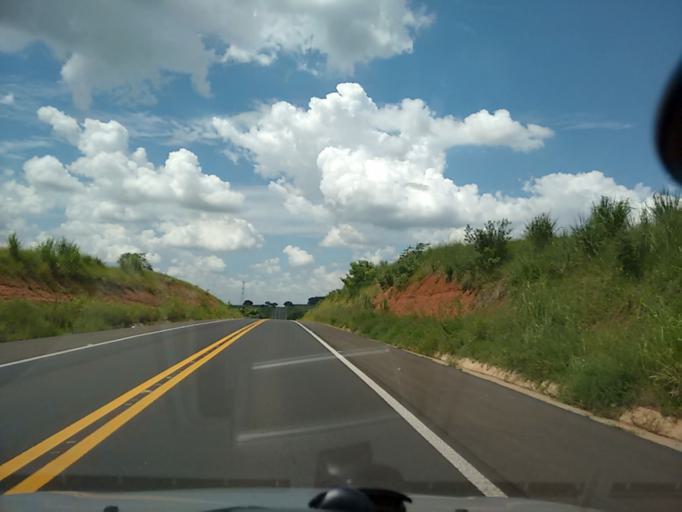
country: BR
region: Sao Paulo
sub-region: Osvaldo Cruz
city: Osvaldo Cruz
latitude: -21.8721
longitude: -50.8563
